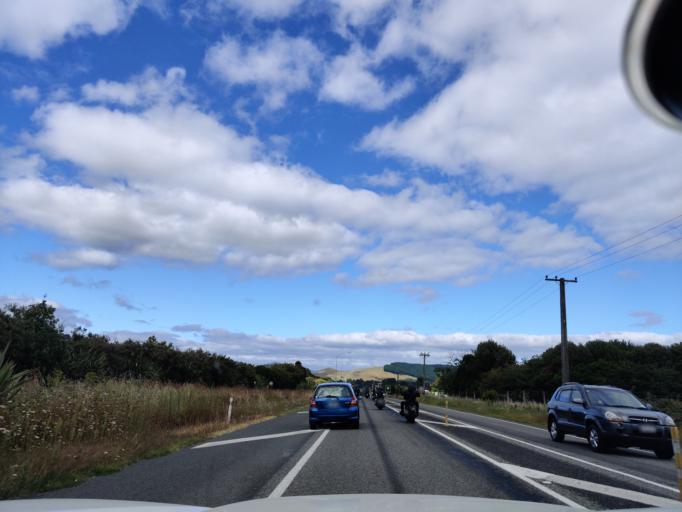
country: NZ
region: Wellington
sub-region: Kapiti Coast District
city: Otaki
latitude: -40.7070
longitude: 175.2197
